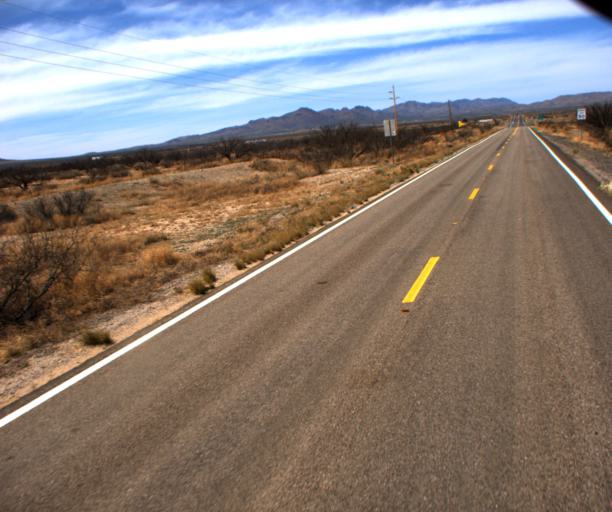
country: US
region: Arizona
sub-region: Cochise County
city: Willcox
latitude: 32.1700
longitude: -109.9462
